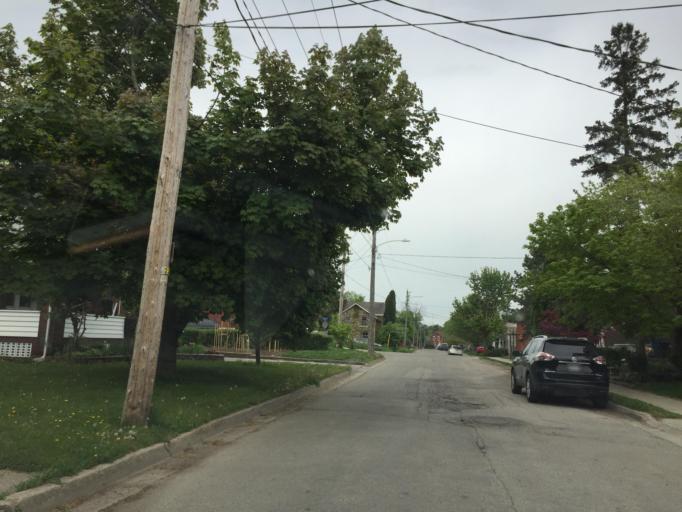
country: CA
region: Ontario
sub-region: Wellington County
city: Guelph
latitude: 43.5438
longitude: -80.2393
